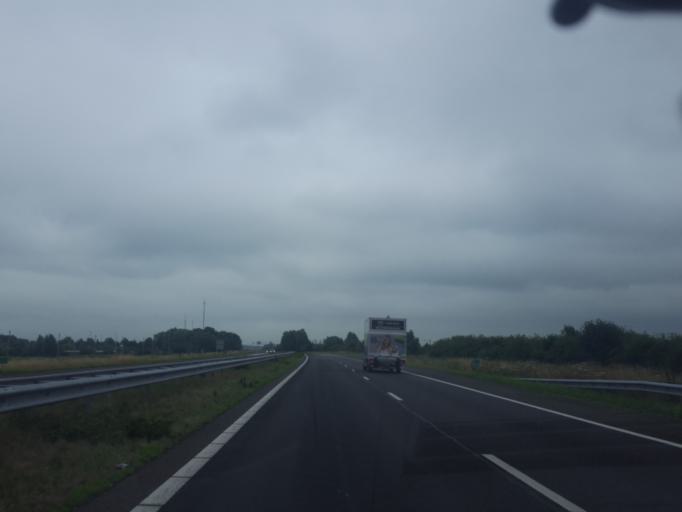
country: NL
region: Friesland
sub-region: Gemeente Boarnsterhim
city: Grou
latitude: 53.0893
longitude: 5.8240
